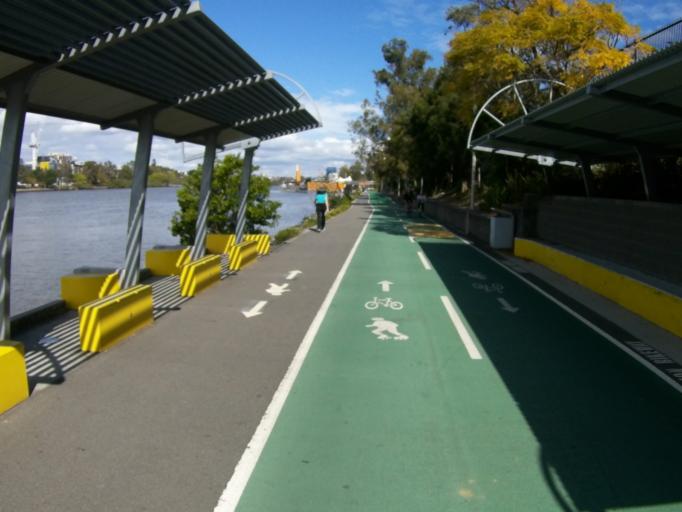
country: AU
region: Queensland
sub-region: Brisbane
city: Milton
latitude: -27.4718
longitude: 153.0073
